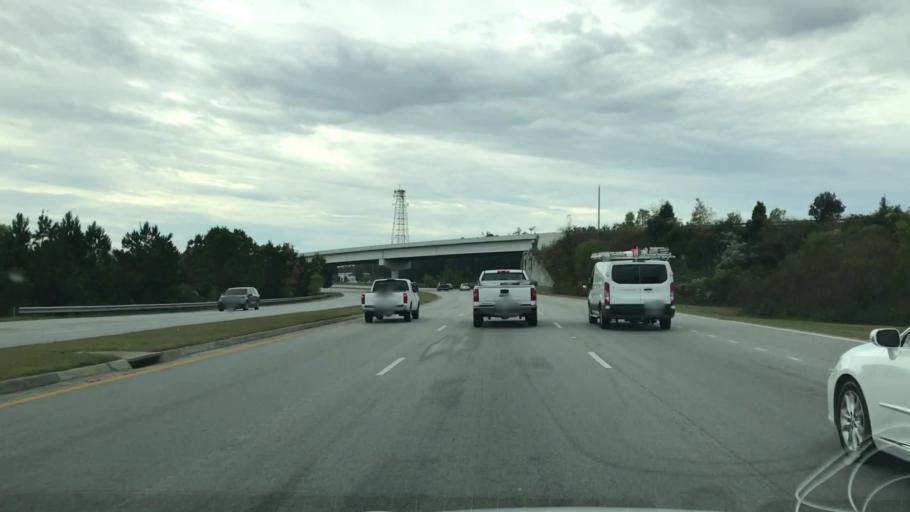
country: US
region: South Carolina
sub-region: Berkeley County
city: Goose Creek
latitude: 32.9730
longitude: -80.0455
